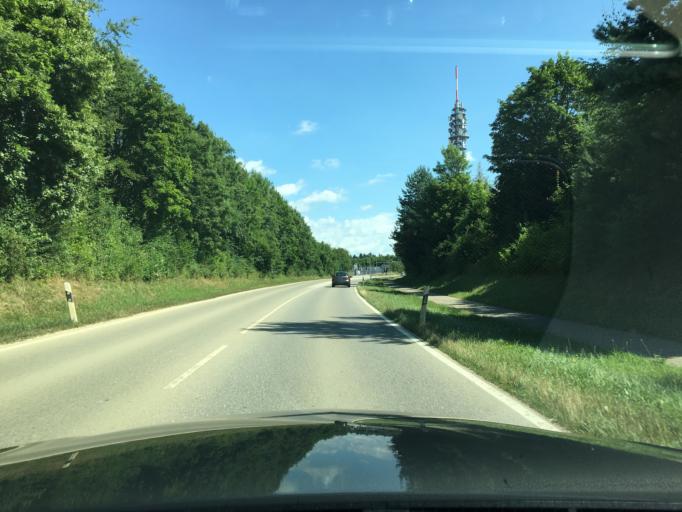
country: DE
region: Baden-Wuerttemberg
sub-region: Tuebingen Region
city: Dornstadt
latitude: 48.4227
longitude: 9.9348
